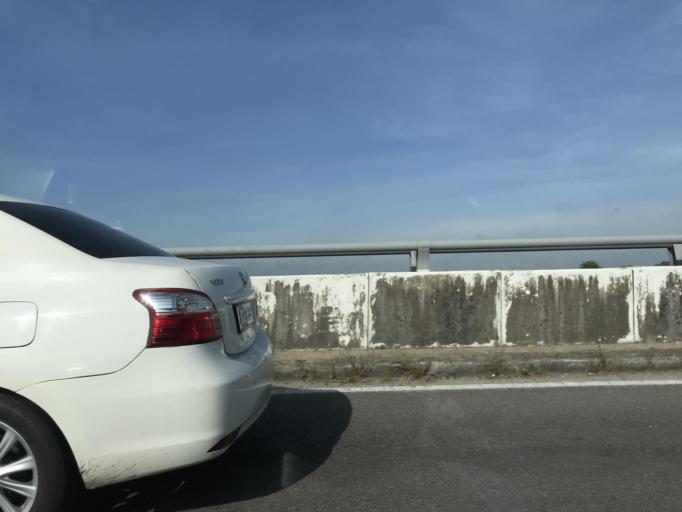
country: MY
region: Kelantan
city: Kampong Kadok
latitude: 6.0569
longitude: 102.2128
